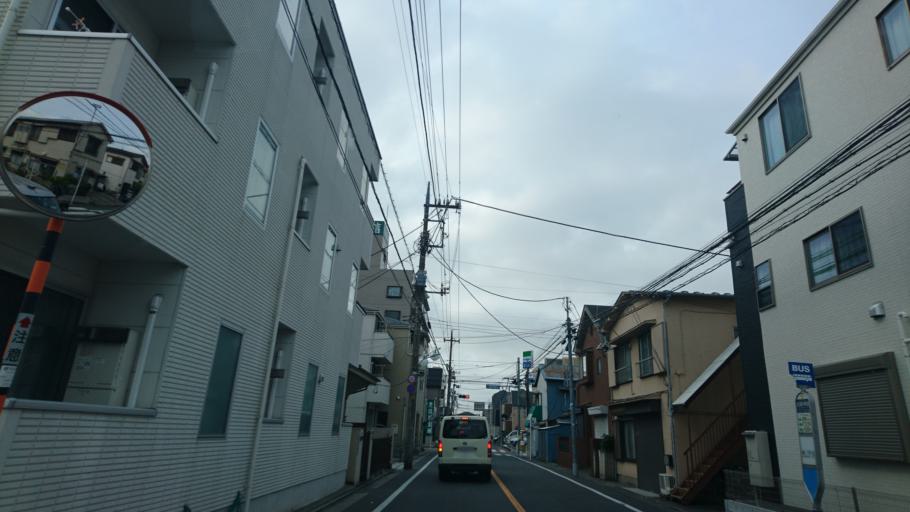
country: JP
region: Kanagawa
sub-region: Kawasaki-shi
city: Kawasaki
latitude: 35.5646
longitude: 139.7045
